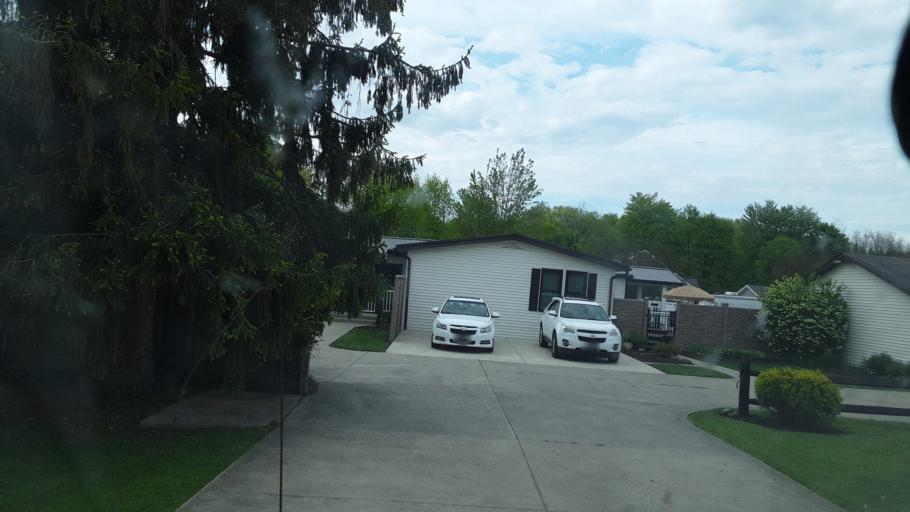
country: US
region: Ohio
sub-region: Portage County
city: Garrettsville
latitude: 41.3029
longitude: -81.0381
